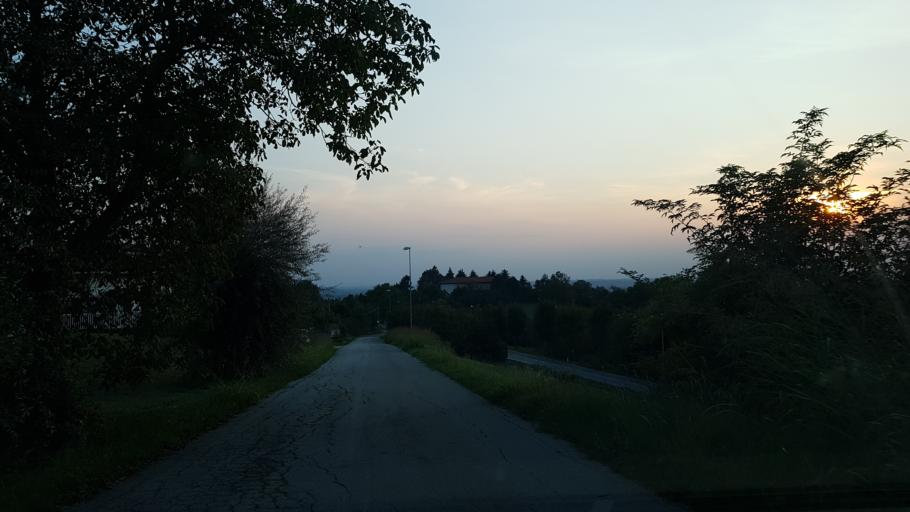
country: IT
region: Piedmont
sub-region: Provincia di Cuneo
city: Novello
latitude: 44.5870
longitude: 7.9245
